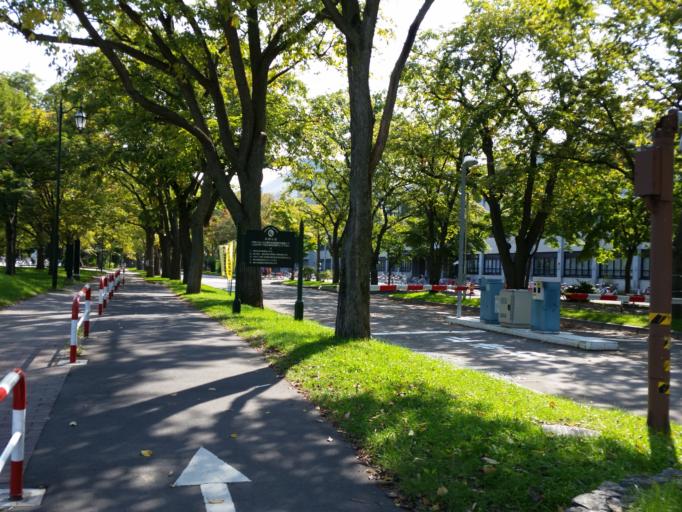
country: JP
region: Hokkaido
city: Sapporo
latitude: 43.0806
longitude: 141.3407
